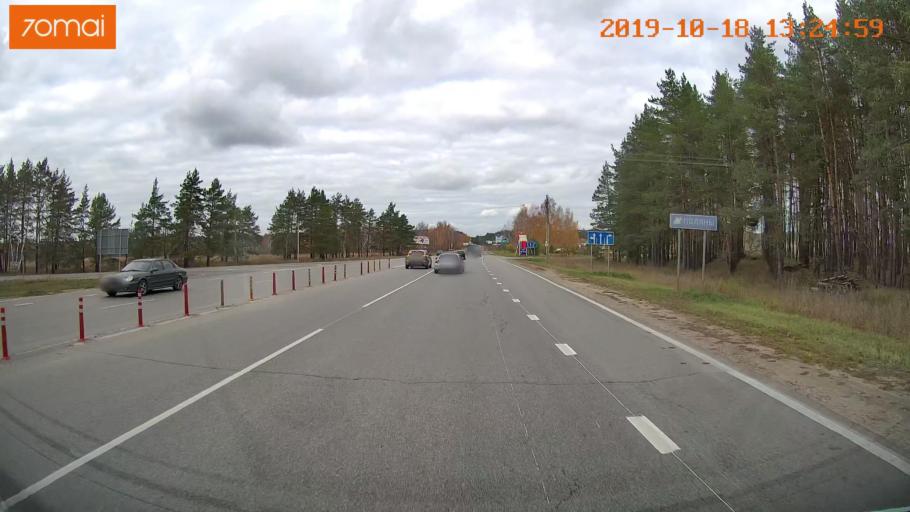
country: RU
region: Rjazan
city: Polyany
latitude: 54.7387
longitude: 39.8411
